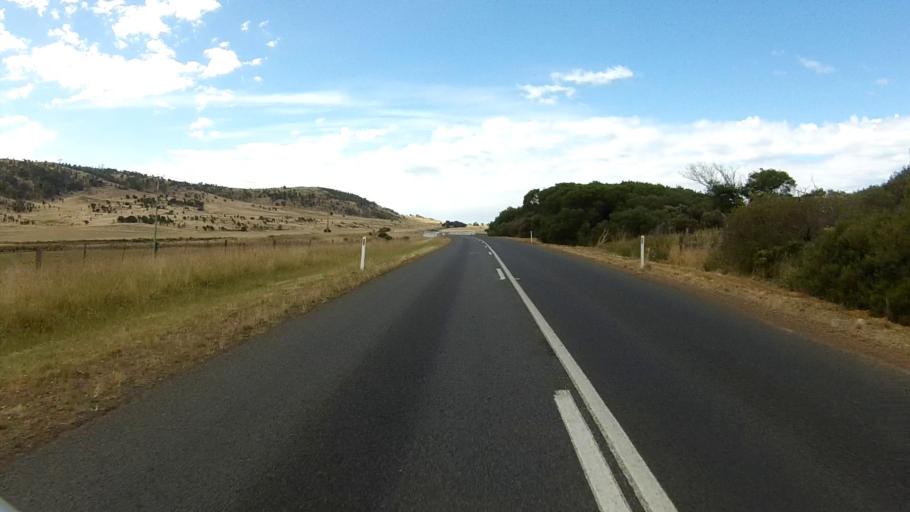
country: AU
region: Tasmania
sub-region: Sorell
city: Sorell
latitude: -42.1994
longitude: 148.0476
